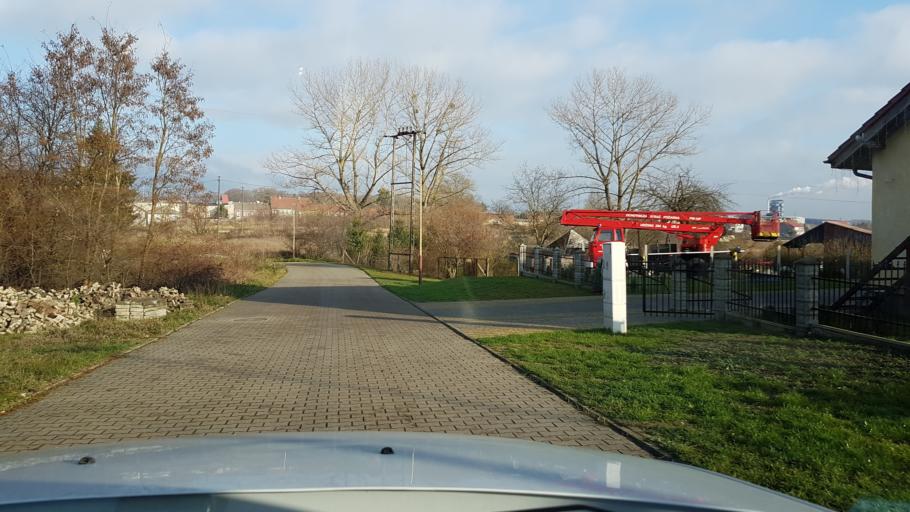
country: PL
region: West Pomeranian Voivodeship
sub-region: Powiat stargardzki
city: Insko
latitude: 53.4331
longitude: 15.5480
